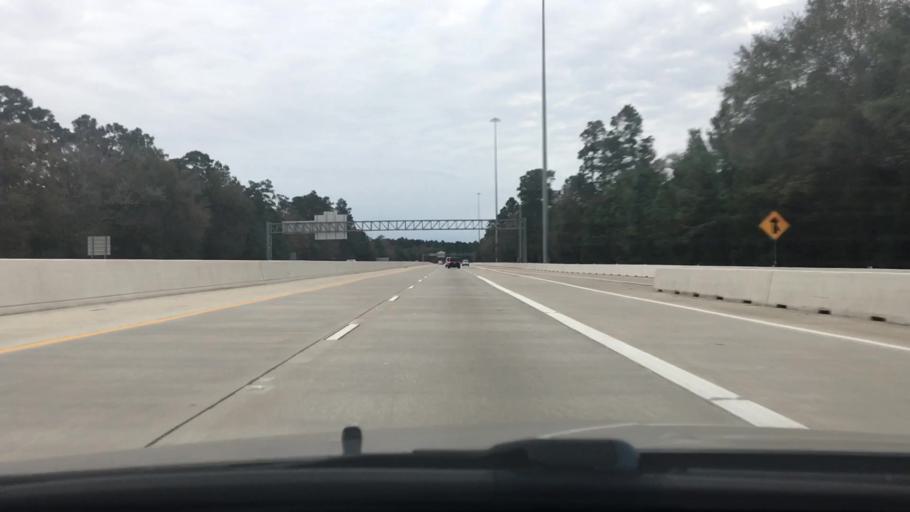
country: US
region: Texas
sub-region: Harris County
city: Spring
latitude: 30.0853
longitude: -95.4123
